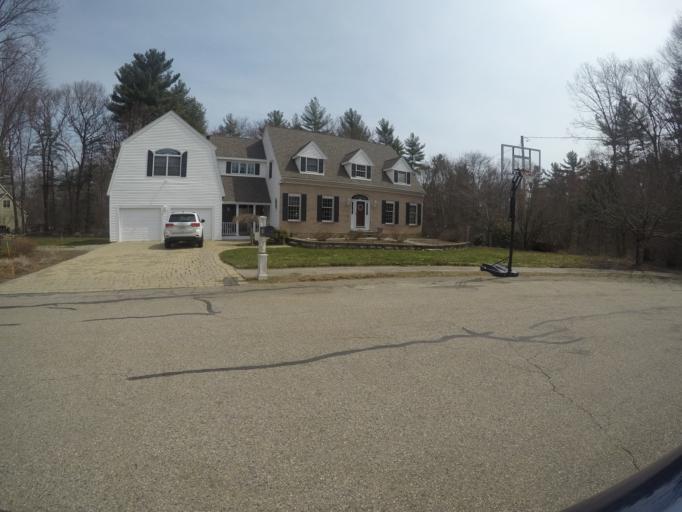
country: US
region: Massachusetts
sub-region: Bristol County
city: Easton
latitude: 42.0382
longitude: -71.1042
